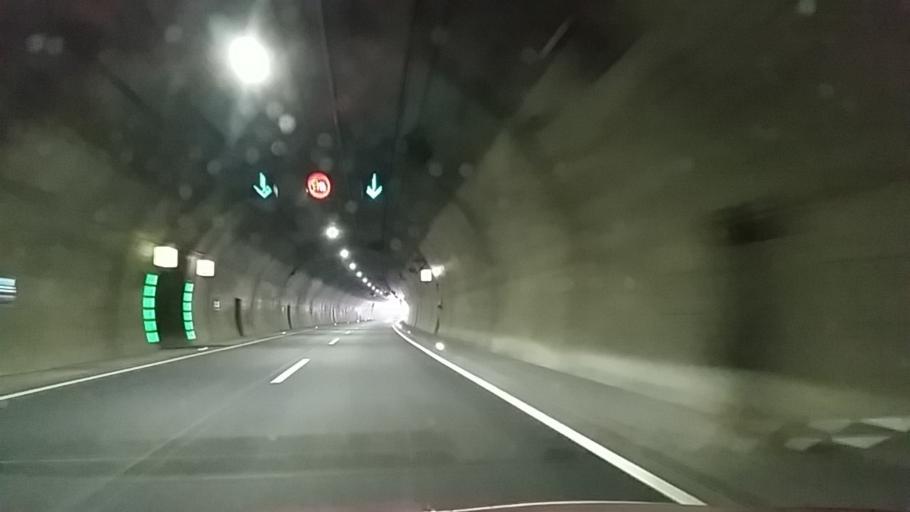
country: DE
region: Thuringia
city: Zella-Mehlis
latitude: 50.6369
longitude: 10.6777
